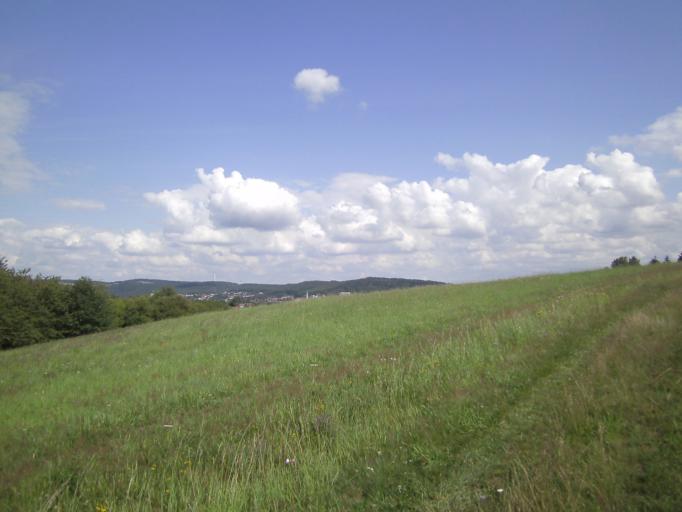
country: DE
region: Saarland
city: Schiffweiler
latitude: 49.3743
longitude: 7.1560
